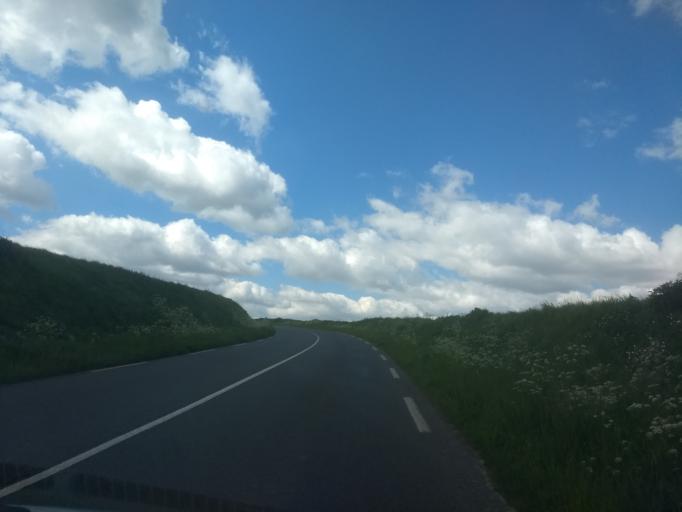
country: FR
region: Nord-Pas-de-Calais
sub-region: Departement du Pas-de-Calais
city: Bailleul-Sir-Berthoult
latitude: 50.3347
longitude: 2.8385
